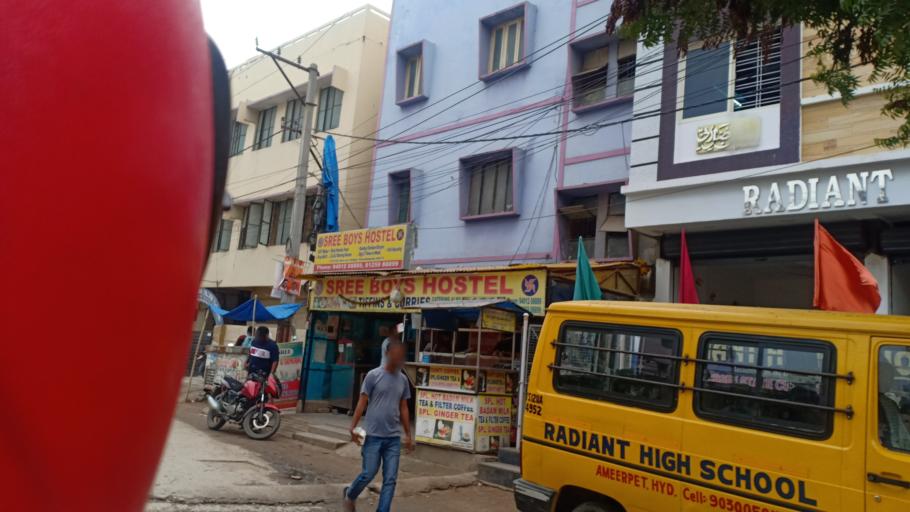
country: IN
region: Telangana
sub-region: Hyderabad
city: Hyderabad
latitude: 17.4332
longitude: 78.4398
